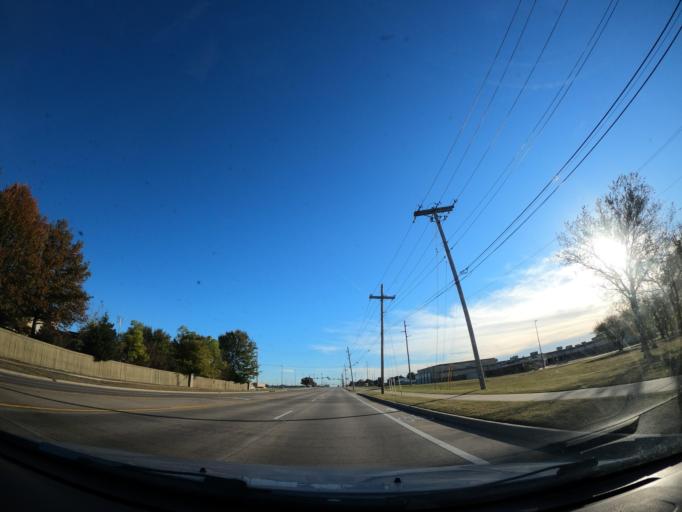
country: US
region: Oklahoma
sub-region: Tulsa County
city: Owasso
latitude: 36.2829
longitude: -95.8303
